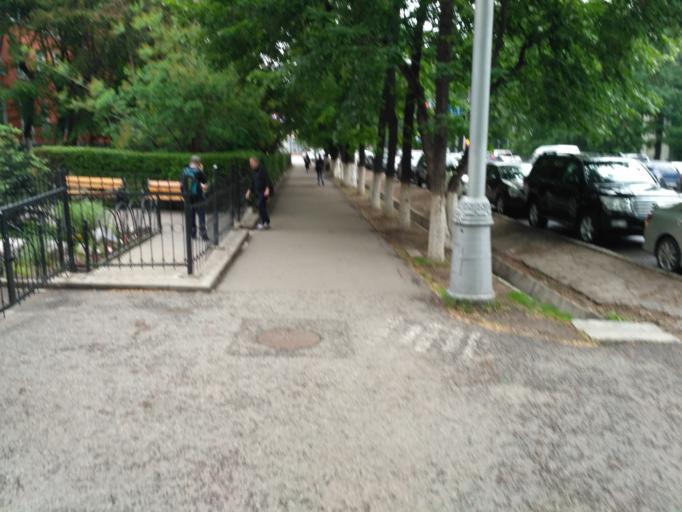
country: KZ
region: Almaty Qalasy
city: Almaty
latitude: 43.2490
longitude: 76.9384
